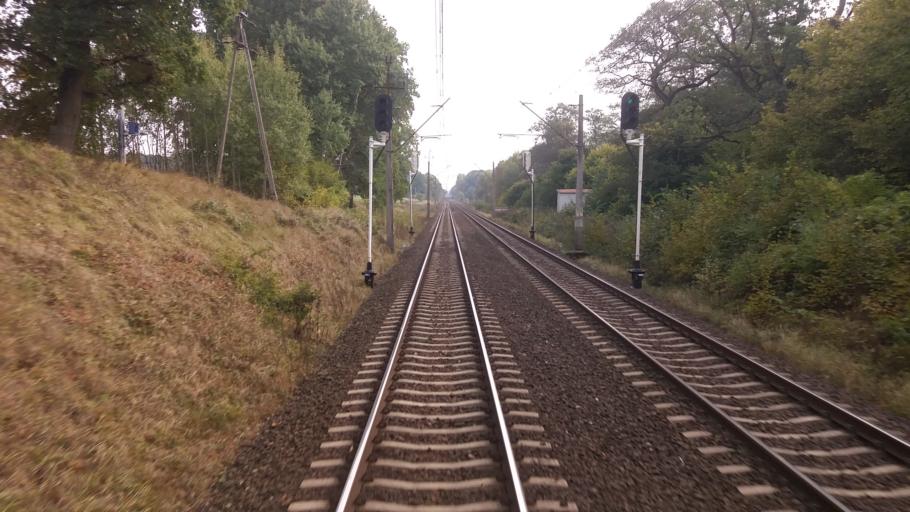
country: PL
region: West Pomeranian Voivodeship
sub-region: Powiat stargardzki
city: Dolice
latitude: 53.1914
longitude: 15.2378
